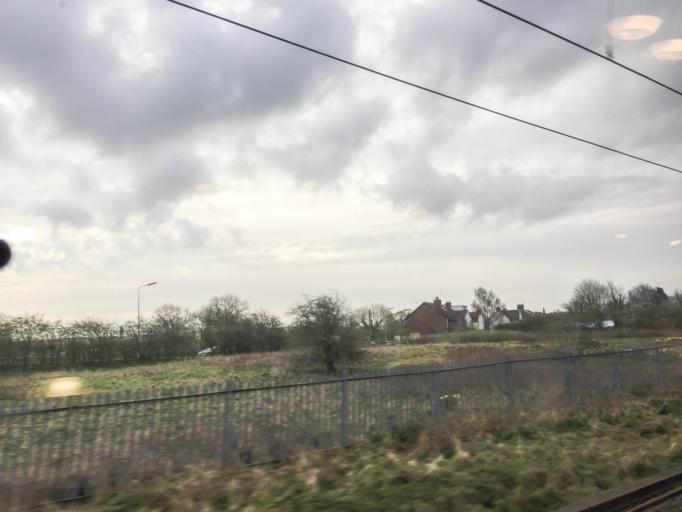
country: GB
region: England
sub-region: Staffordshire
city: Stafford
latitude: 52.7737
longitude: -2.1110
